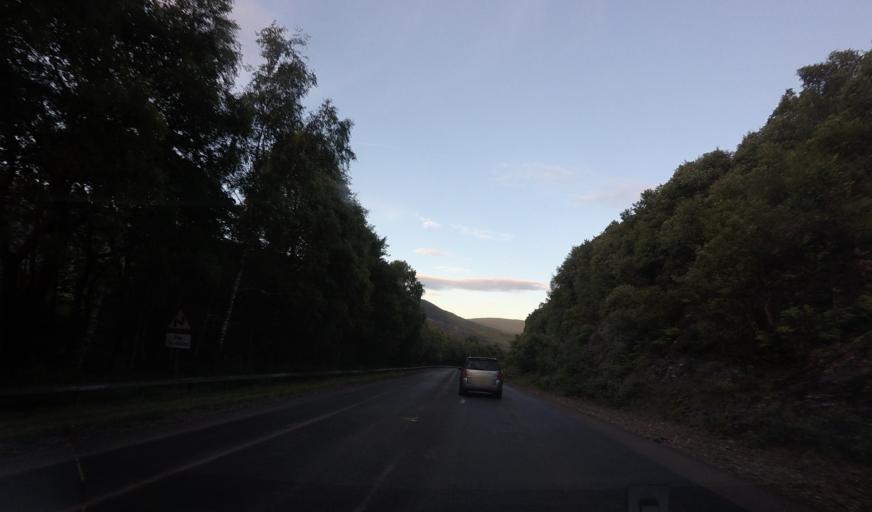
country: GB
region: Scotland
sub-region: Argyll and Bute
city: Helensburgh
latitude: 56.1681
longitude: -4.6732
